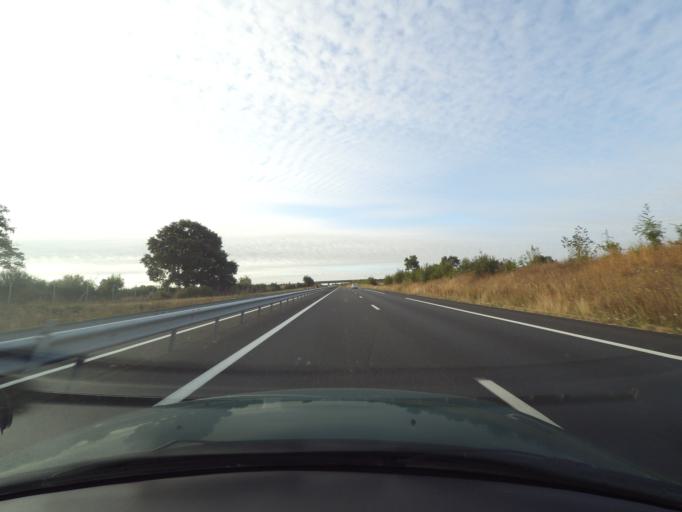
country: FR
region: Pays de la Loire
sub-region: Departement de Maine-et-Loire
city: La Tessoualle
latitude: 47.0066
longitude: -0.8682
